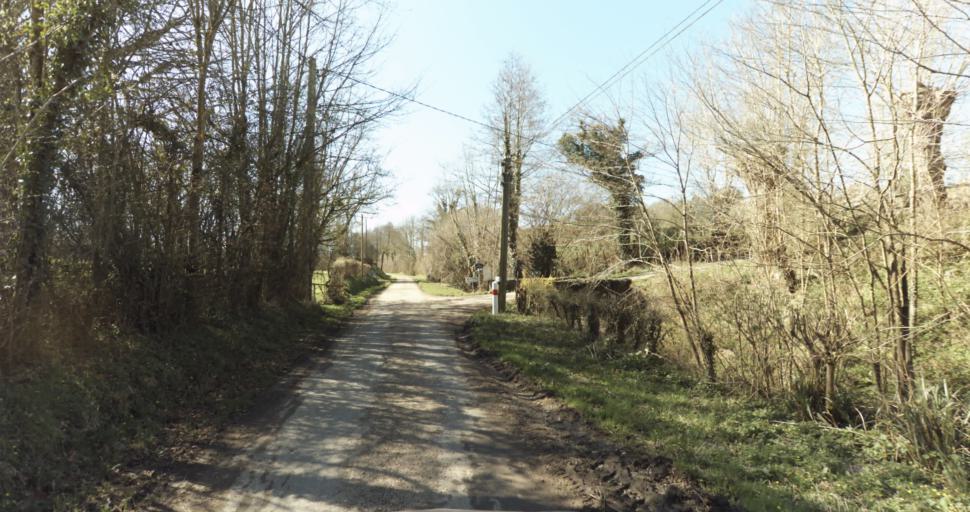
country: FR
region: Lower Normandy
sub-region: Departement du Calvados
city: Livarot
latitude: 48.9522
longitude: 0.0742
